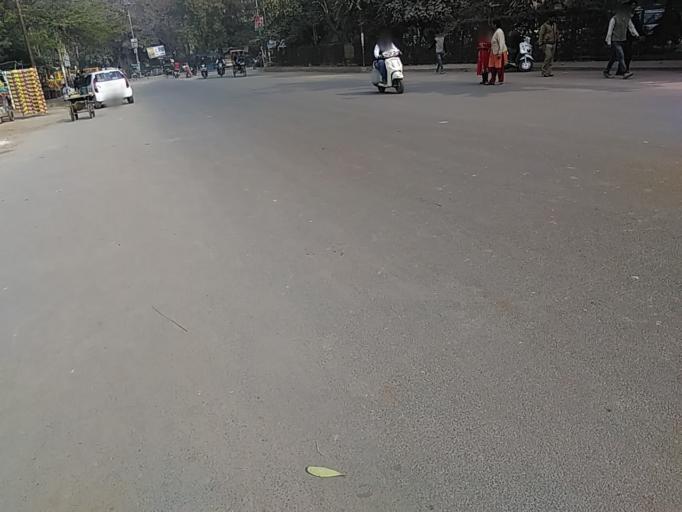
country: IN
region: Uttar Pradesh
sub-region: Gautam Buddha Nagar
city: Noida
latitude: 28.6426
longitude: 77.3194
